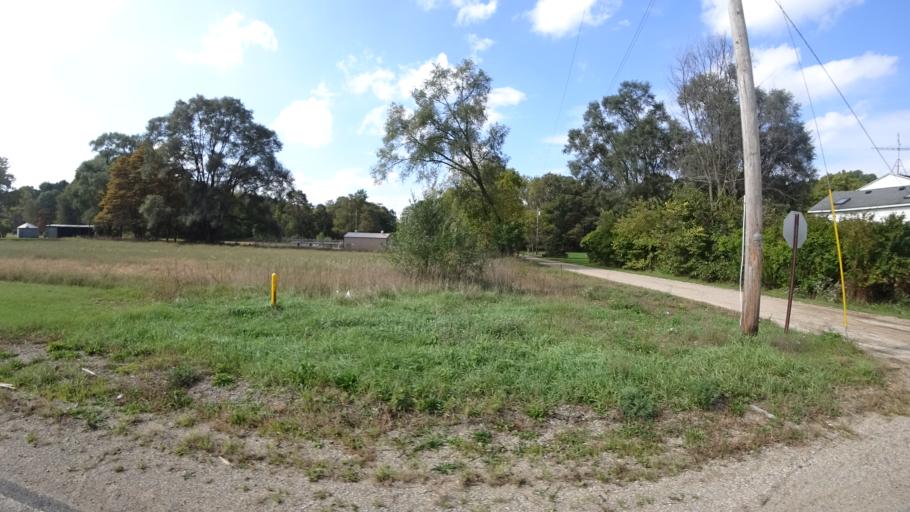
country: US
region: Michigan
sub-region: Saint Joseph County
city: Three Rivers
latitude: 41.9181
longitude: -85.6246
